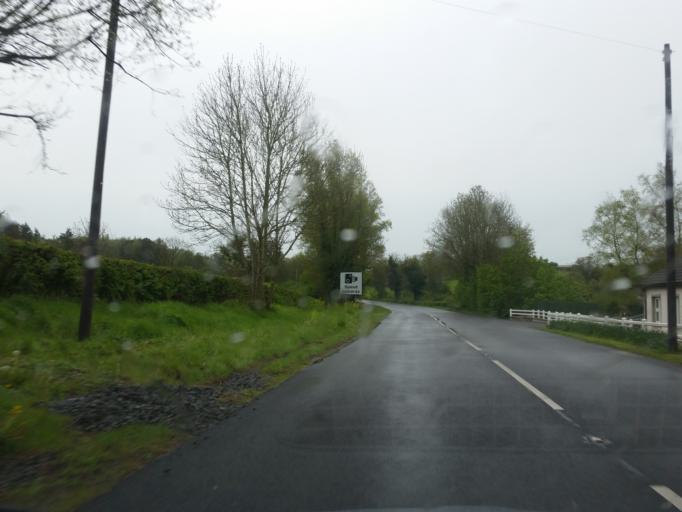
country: GB
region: Northern Ireland
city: Lisnaskea
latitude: 54.2350
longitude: -7.4229
